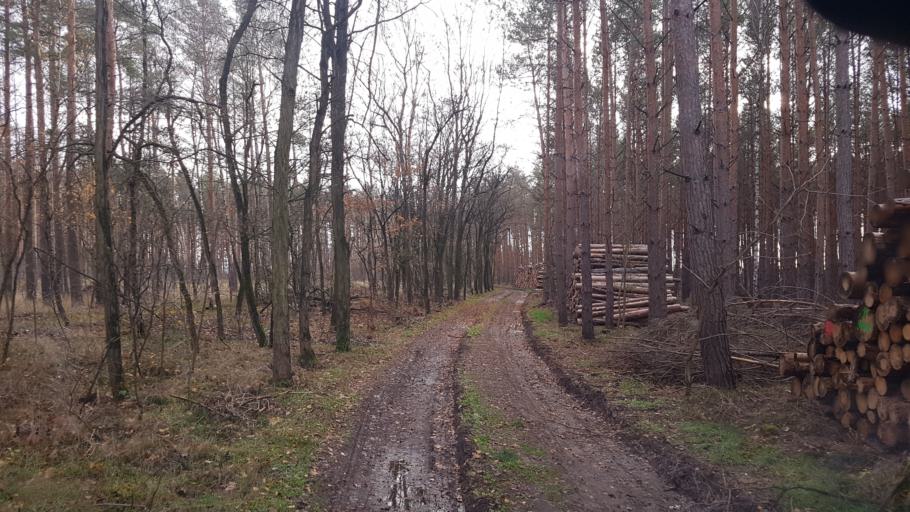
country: DE
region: Brandenburg
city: Falkenberg
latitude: 51.5616
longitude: 13.2892
